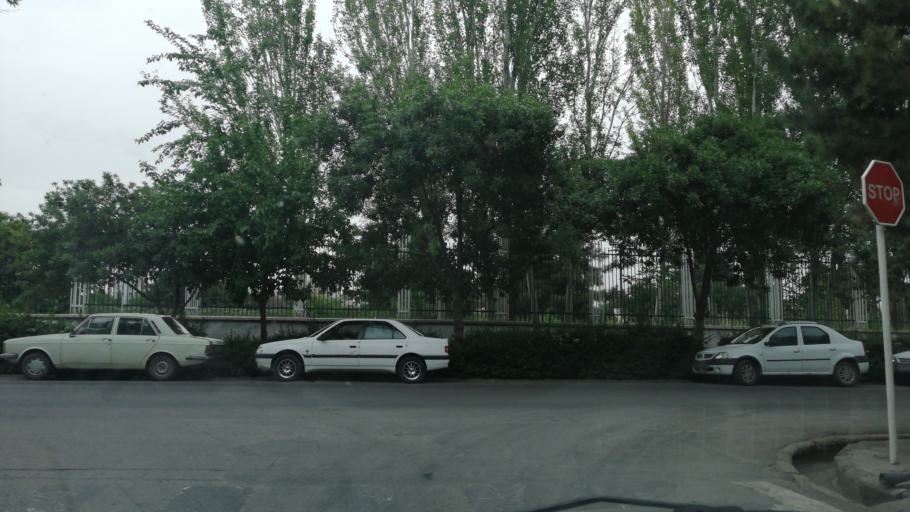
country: IR
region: Razavi Khorasan
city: Mashhad
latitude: 36.2870
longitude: 59.5779
